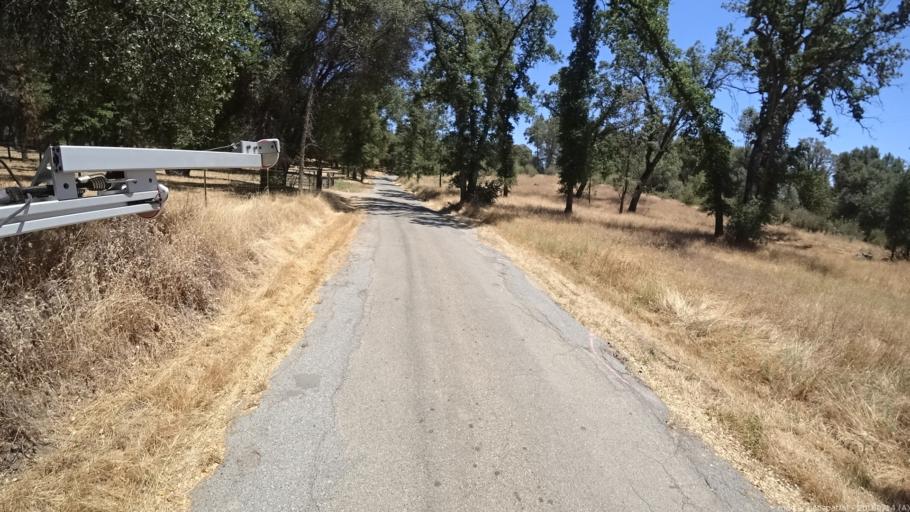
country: US
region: California
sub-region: Madera County
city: Ahwahnee
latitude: 37.3959
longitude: -119.7403
